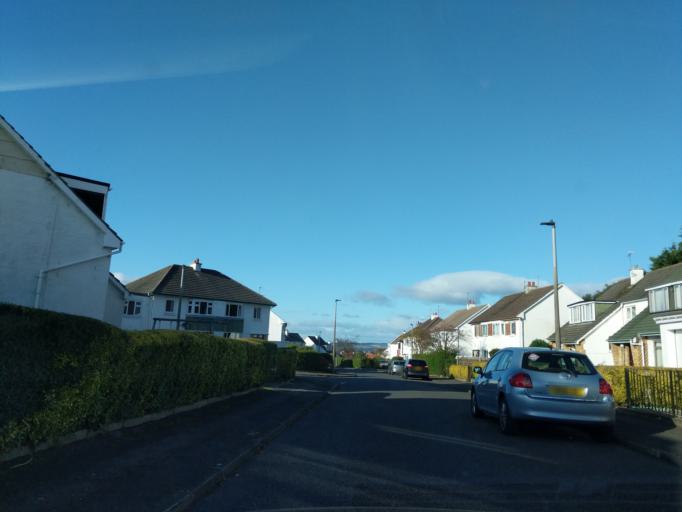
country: GB
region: Scotland
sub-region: Edinburgh
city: Colinton
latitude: 55.9675
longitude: -3.2648
